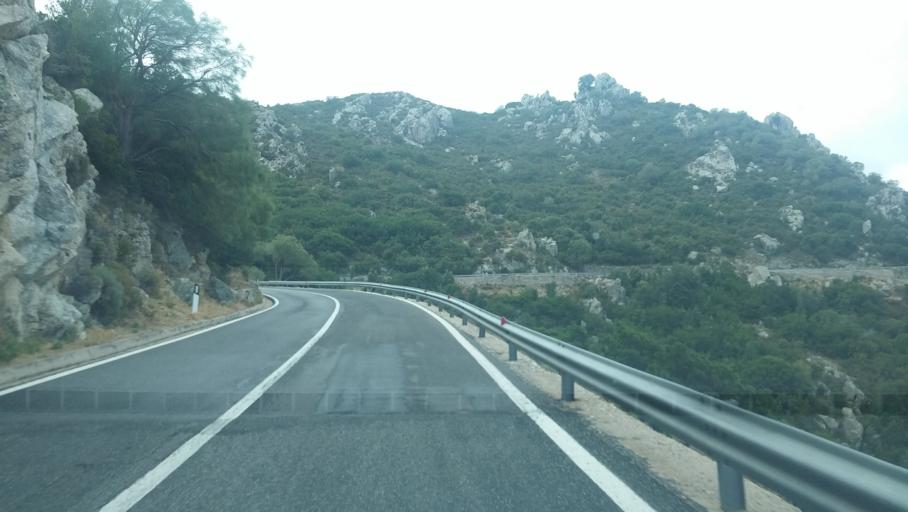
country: IT
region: Sardinia
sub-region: Provincia di Ogliastra
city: Urzulei
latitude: 40.1808
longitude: 9.5328
